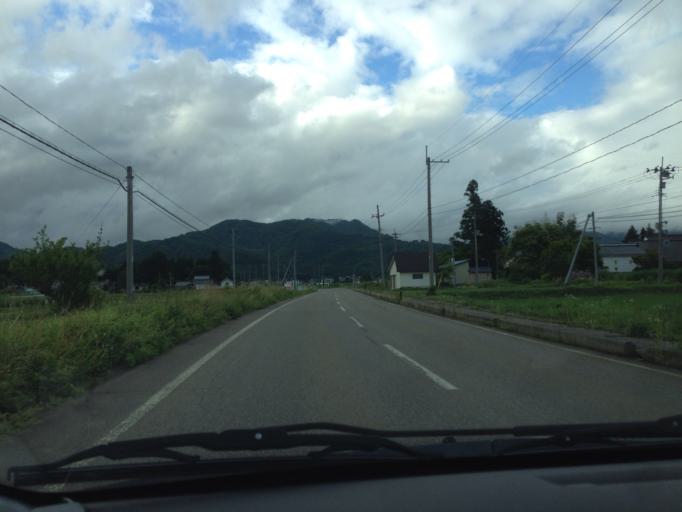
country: JP
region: Fukushima
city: Kitakata
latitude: 37.7104
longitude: 139.8558
